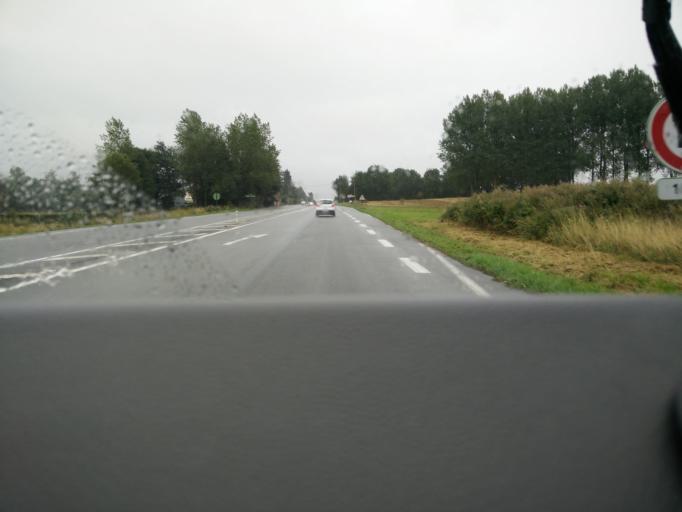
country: FR
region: Nord-Pas-de-Calais
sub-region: Departement du Pas-de-Calais
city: Saint-Pol-sur-Ternoise
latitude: 50.3822
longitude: 2.2701
